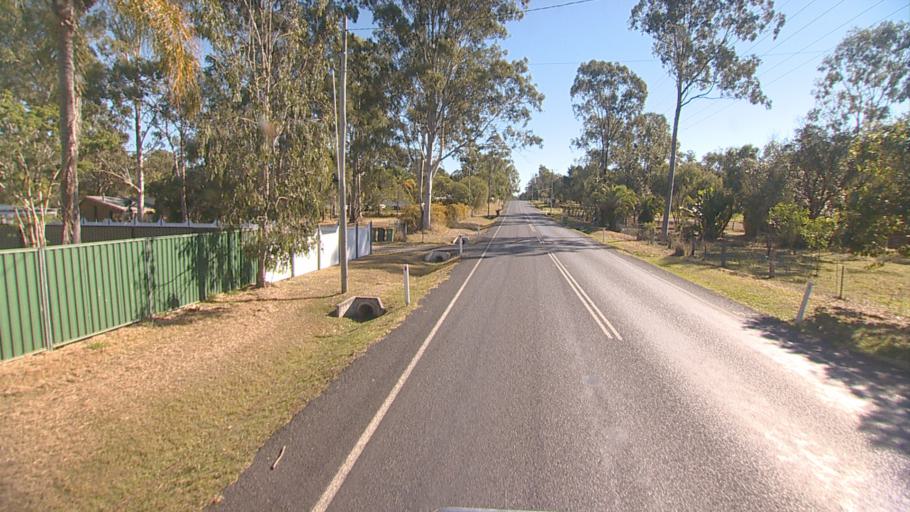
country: AU
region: Queensland
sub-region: Logan
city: Park Ridge South
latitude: -27.7237
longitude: 153.0086
